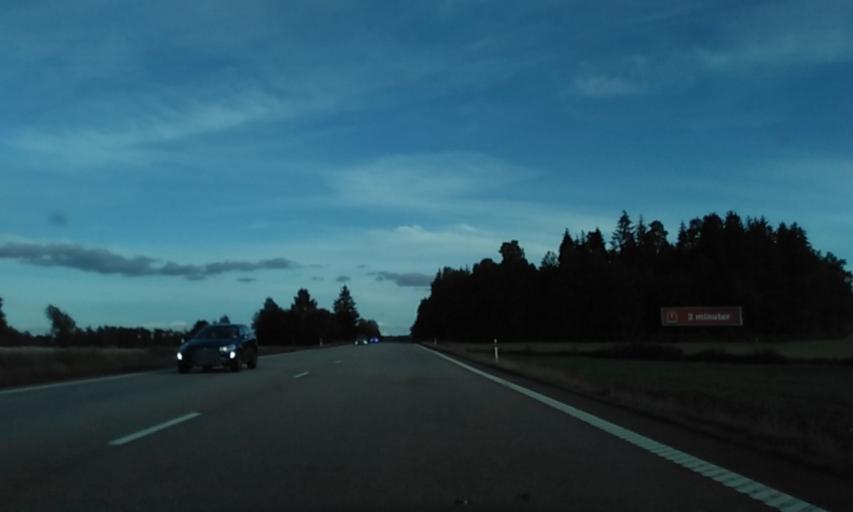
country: SE
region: Vaestra Goetaland
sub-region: Vargarda Kommun
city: Vargarda
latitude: 58.0658
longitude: 12.8168
